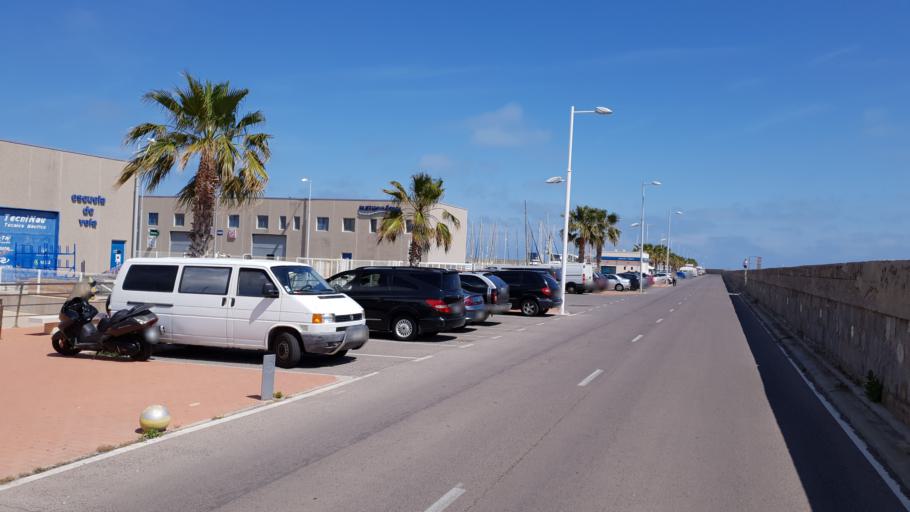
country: ES
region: Valencia
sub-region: Provincia de Castello
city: Burriana
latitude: 39.8610
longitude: -0.0740
